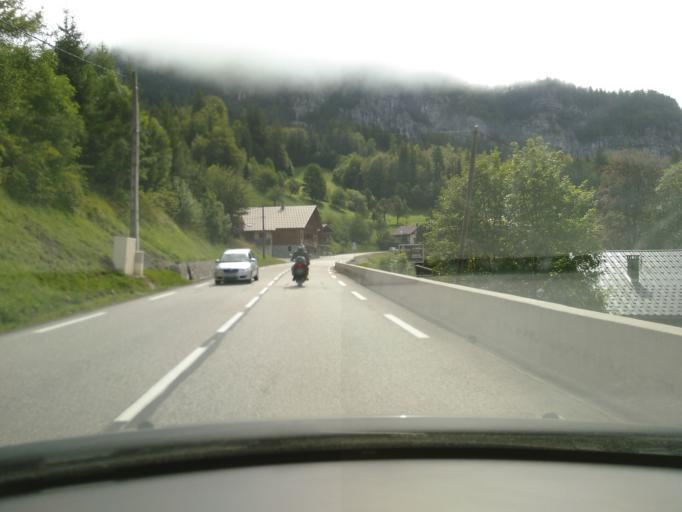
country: FR
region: Rhone-Alpes
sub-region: Departement de la Haute-Savoie
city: Saint-Jean-de-Sixt
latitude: 45.9177
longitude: 6.4182
